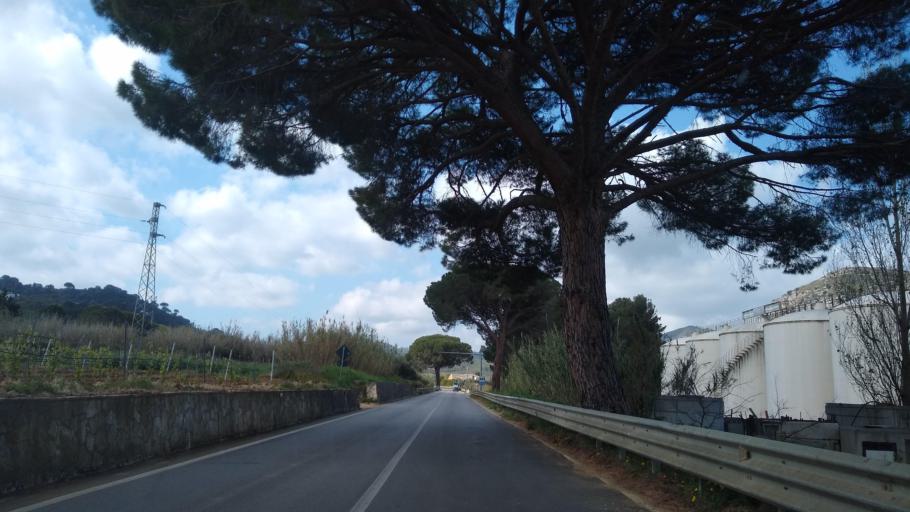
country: IT
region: Sicily
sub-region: Trapani
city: Calatafimi
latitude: 37.9419
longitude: 12.8577
